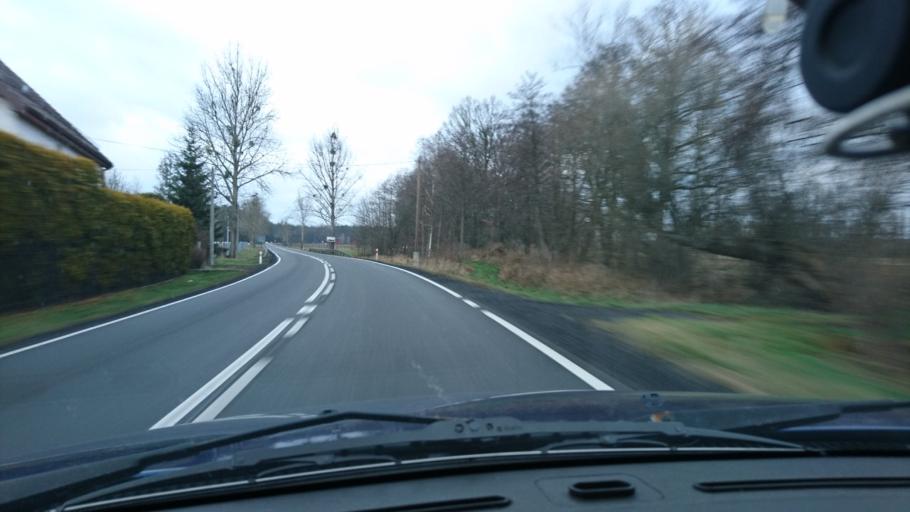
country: PL
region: Opole Voivodeship
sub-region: Powiat oleski
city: Olesno
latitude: 50.9162
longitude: 18.3466
